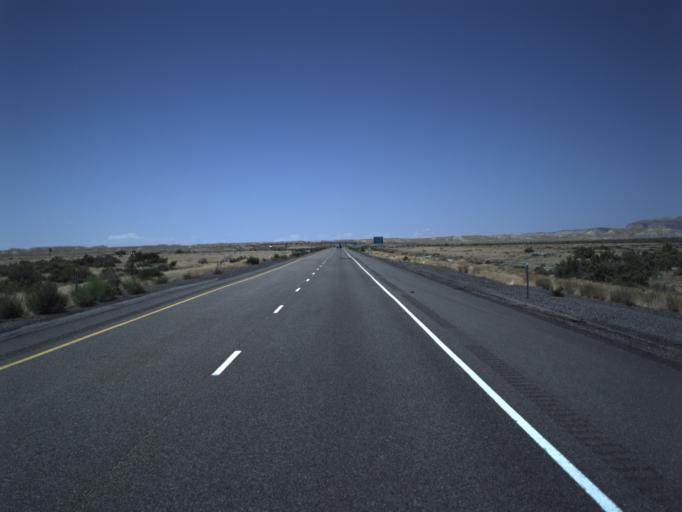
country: US
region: Utah
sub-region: Grand County
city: Moab
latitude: 38.9428
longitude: -109.5963
